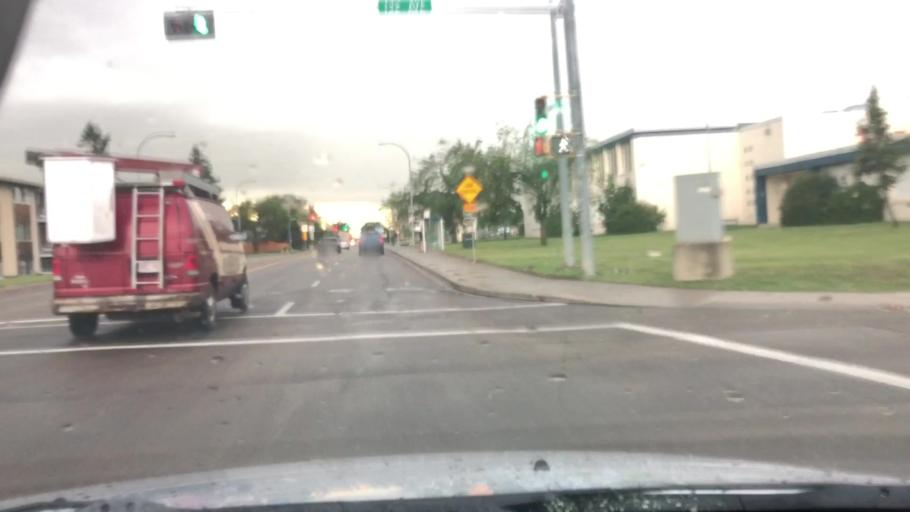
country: CA
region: Alberta
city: Edmonton
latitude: 53.5922
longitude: -113.5413
